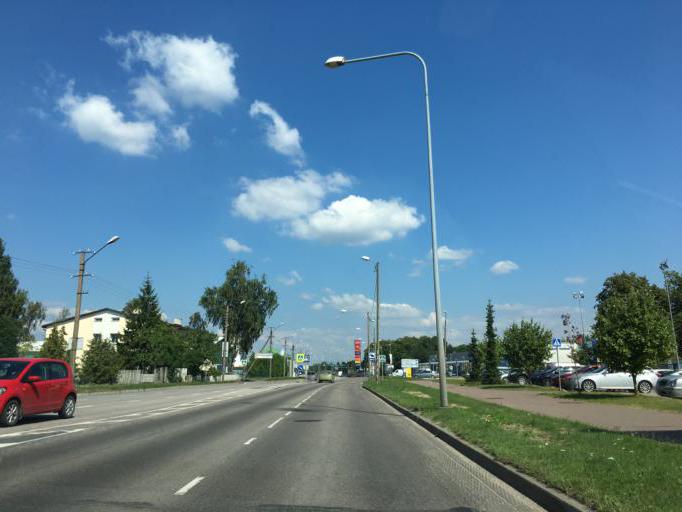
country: EE
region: Paernumaa
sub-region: Paernu linn
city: Parnu
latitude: 58.3715
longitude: 24.5499
